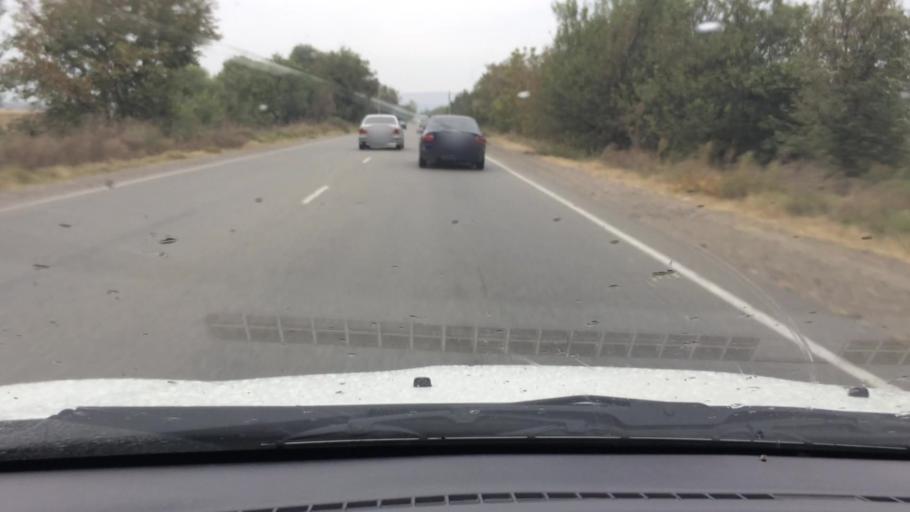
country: GE
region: Kvemo Kartli
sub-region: Marneuli
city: Marneuli
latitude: 41.5600
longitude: 44.7759
